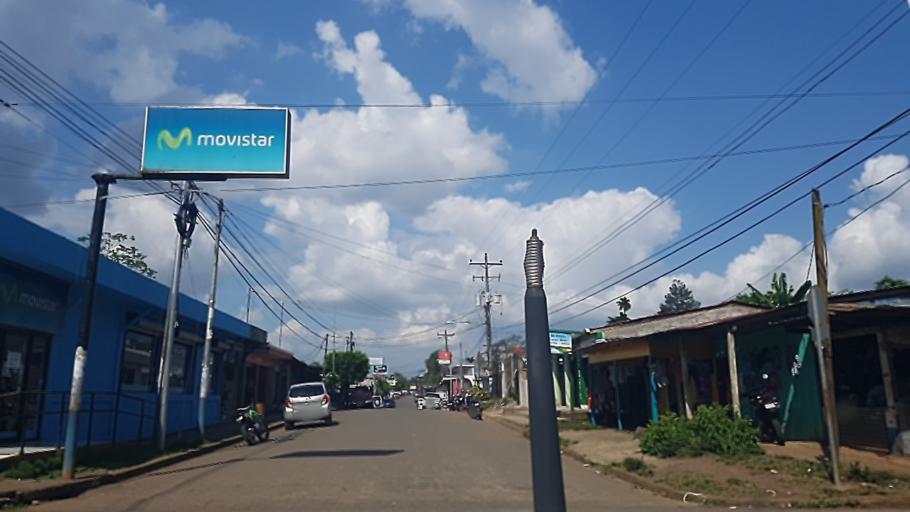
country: NI
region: Atlantico Sur
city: Nueva Guinea
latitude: 11.6885
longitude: -84.4566
